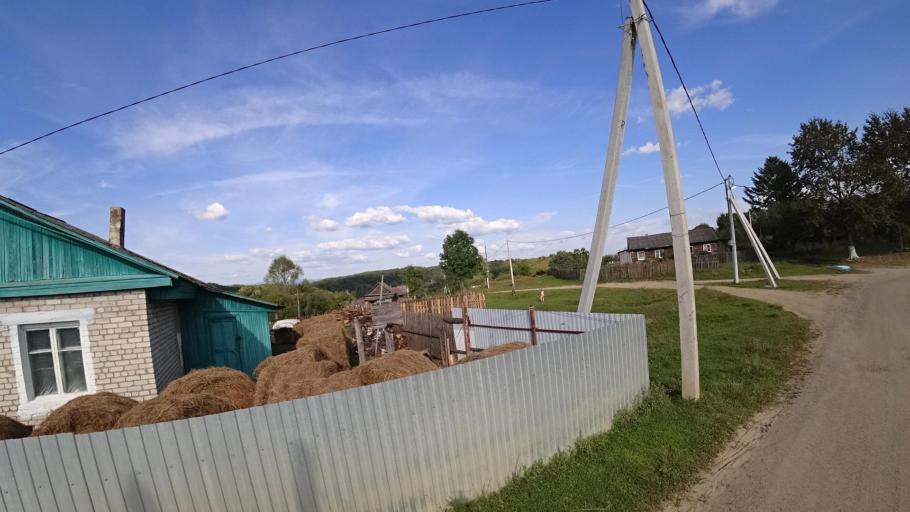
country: RU
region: Jewish Autonomous Oblast
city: Birakan
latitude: 48.9999
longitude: 131.7115
